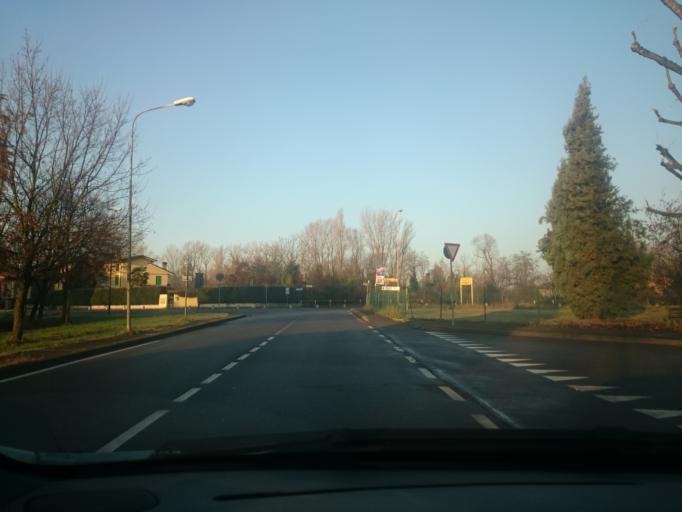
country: IT
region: Emilia-Romagna
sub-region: Provincia di Reggio Emilia
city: Fellegara
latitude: 44.6063
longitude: 10.6922
